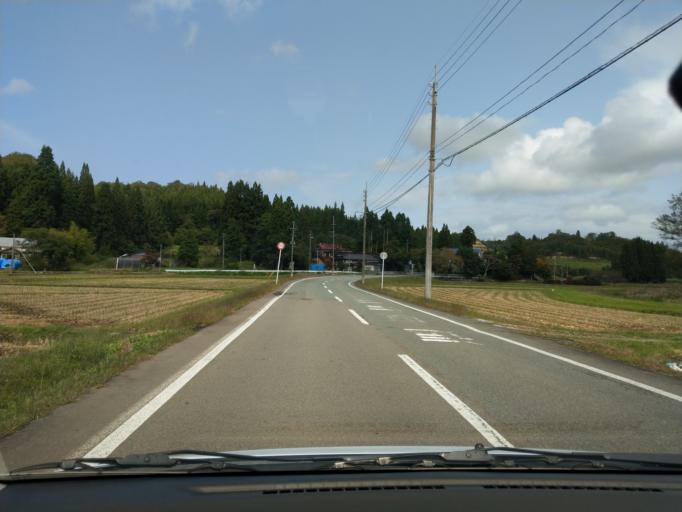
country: JP
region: Akita
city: Omagari
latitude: 39.5048
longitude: 140.3123
